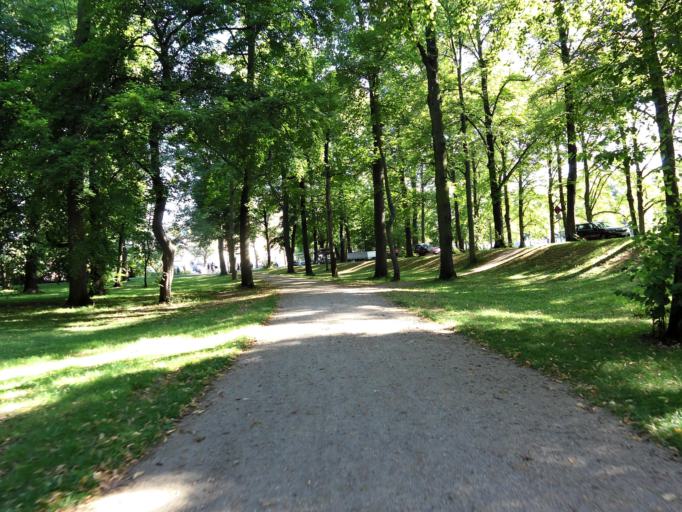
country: DE
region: Saxony
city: Leipzig
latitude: 51.3273
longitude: 12.3567
